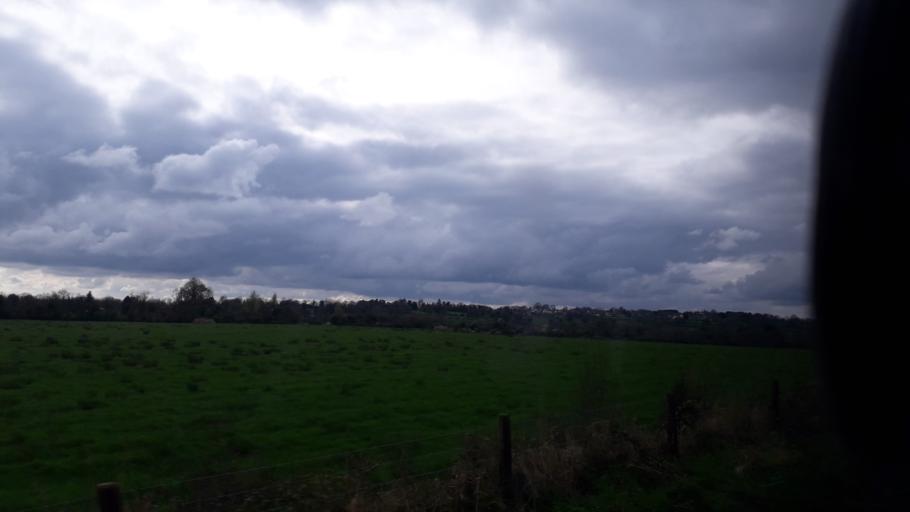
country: IE
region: Leinster
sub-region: An Longfort
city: Longford
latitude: 53.7131
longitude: -7.7468
